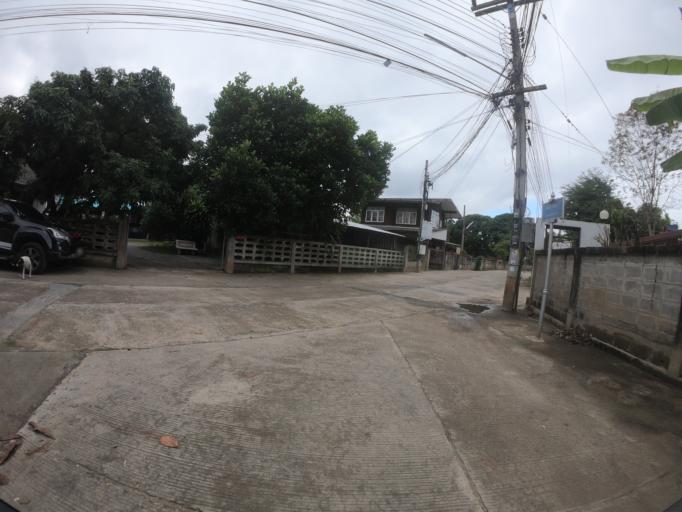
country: TH
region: Chiang Mai
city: Hang Dong
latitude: 18.7064
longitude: 98.9593
